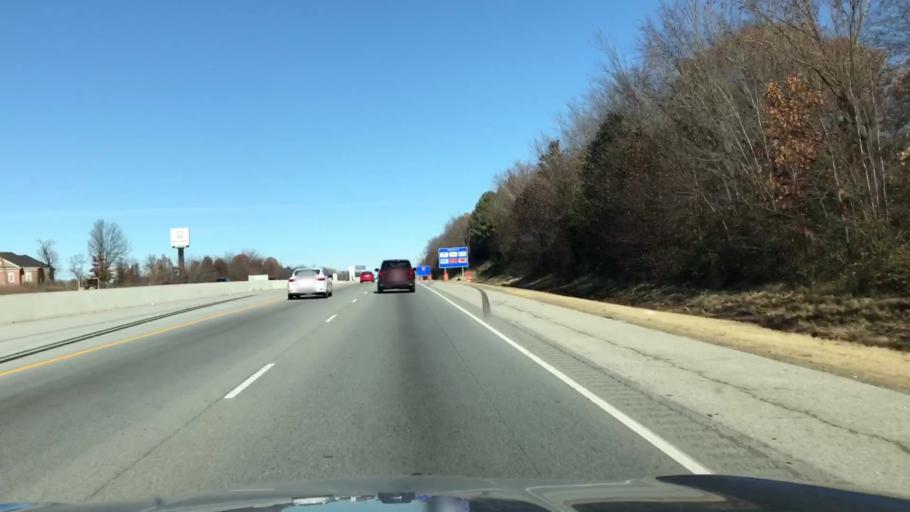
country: US
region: Arkansas
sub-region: Benton County
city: Bentonville
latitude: 36.3246
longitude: -94.1847
